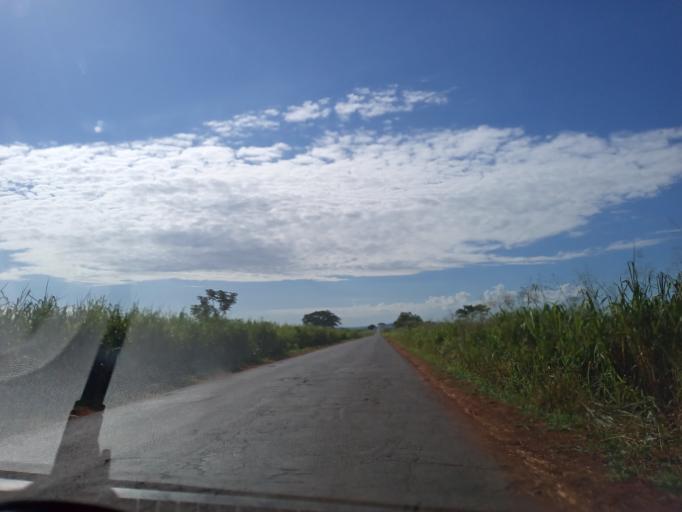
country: BR
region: Goias
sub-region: Itumbiara
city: Itumbiara
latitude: -18.4460
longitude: -49.1713
